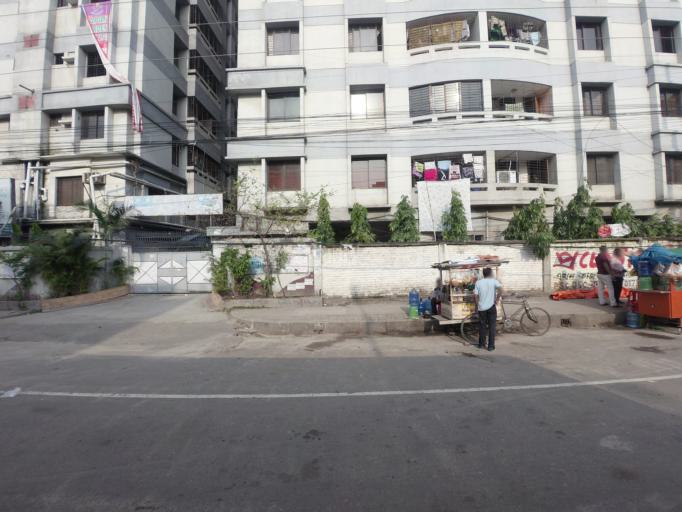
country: BD
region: Dhaka
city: Azimpur
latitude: 23.7644
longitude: 90.3584
